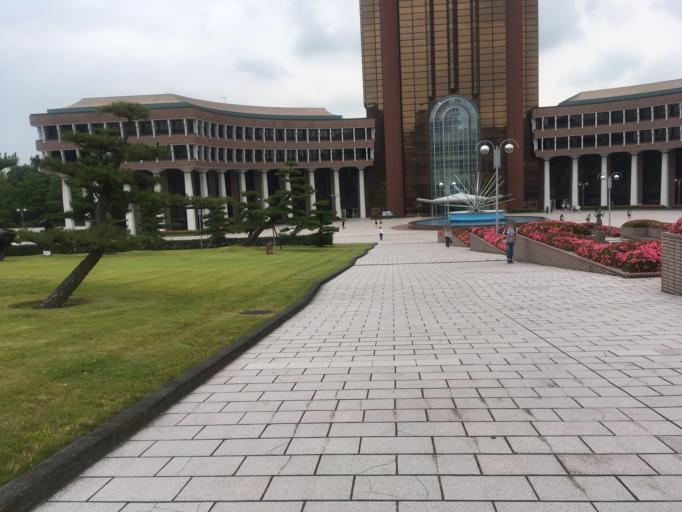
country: JP
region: Tokyo
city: Hachioji
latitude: 35.6265
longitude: 139.3407
